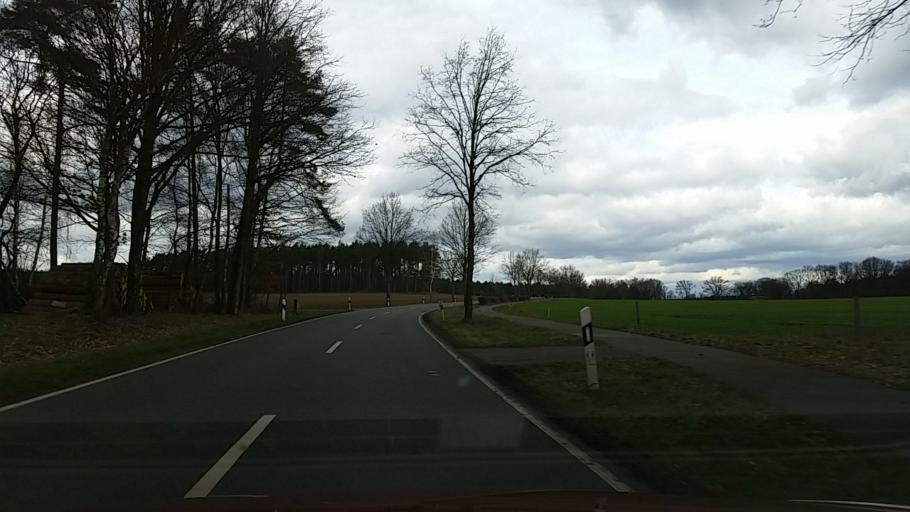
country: DE
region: Lower Saxony
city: Zernien
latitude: 53.0926
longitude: 10.9452
